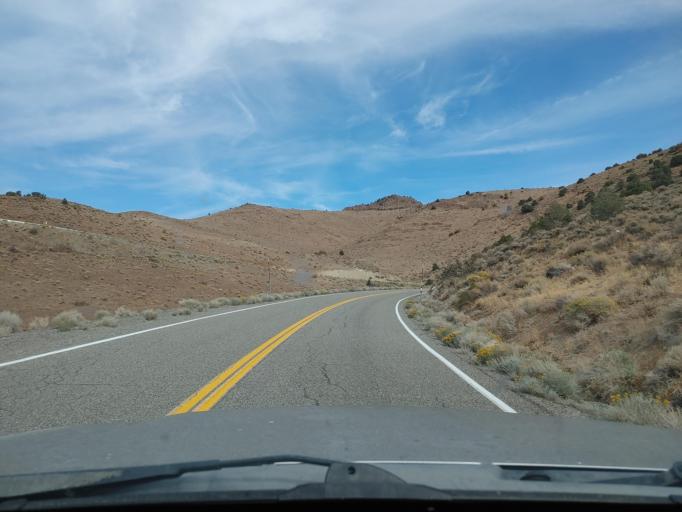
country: US
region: Nevada
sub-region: Storey County
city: Virginia City
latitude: 39.2705
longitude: -119.6281
